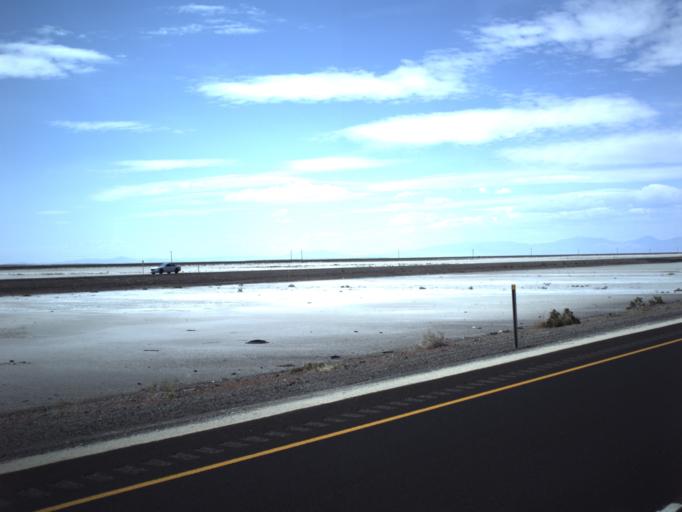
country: US
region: Utah
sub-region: Tooele County
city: Wendover
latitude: 40.7321
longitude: -113.5110
